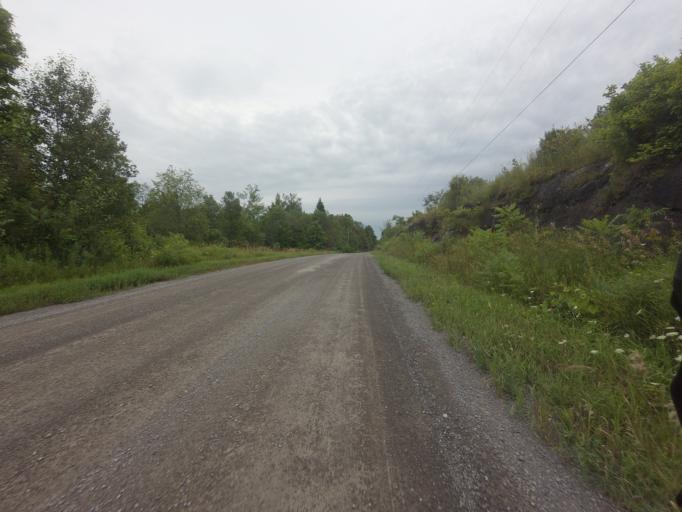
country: CA
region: Ontario
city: Carleton Place
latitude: 45.1608
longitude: -76.2691
